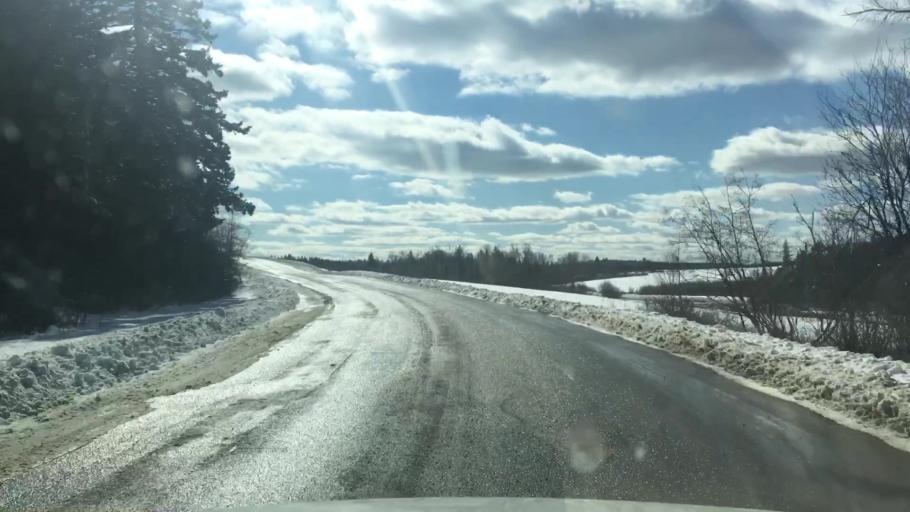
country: US
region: Maine
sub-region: Washington County
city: Machiasport
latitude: 44.6738
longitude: -67.4221
